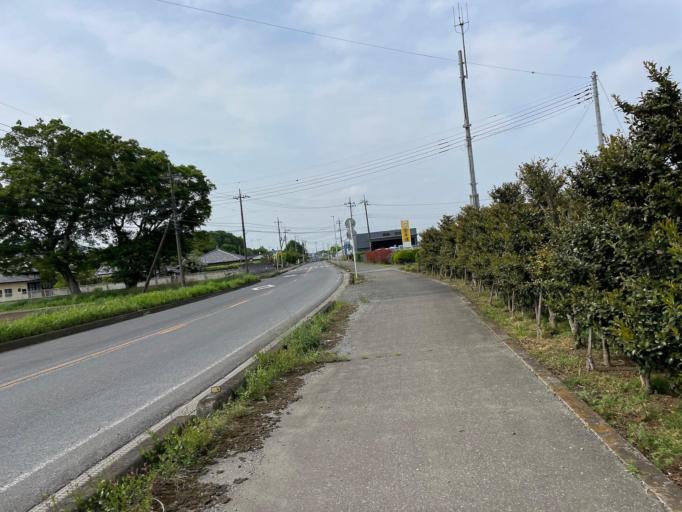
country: JP
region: Tochigi
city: Mibu
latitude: 36.3846
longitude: 139.8047
